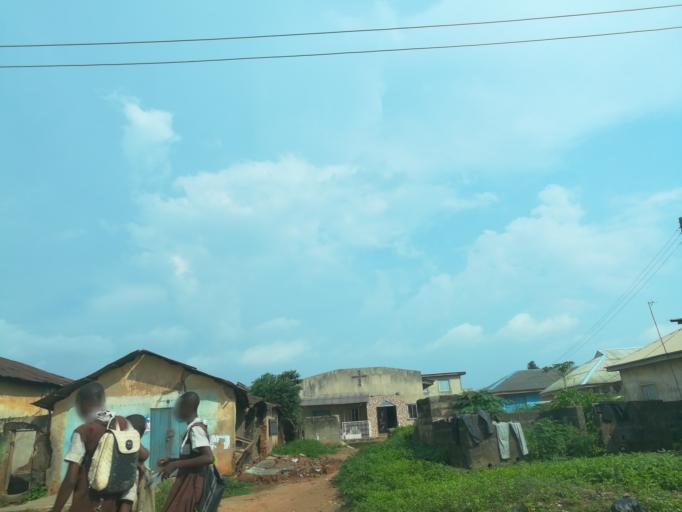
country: NG
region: Lagos
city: Ikorodu
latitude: 6.6662
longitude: 3.6724
